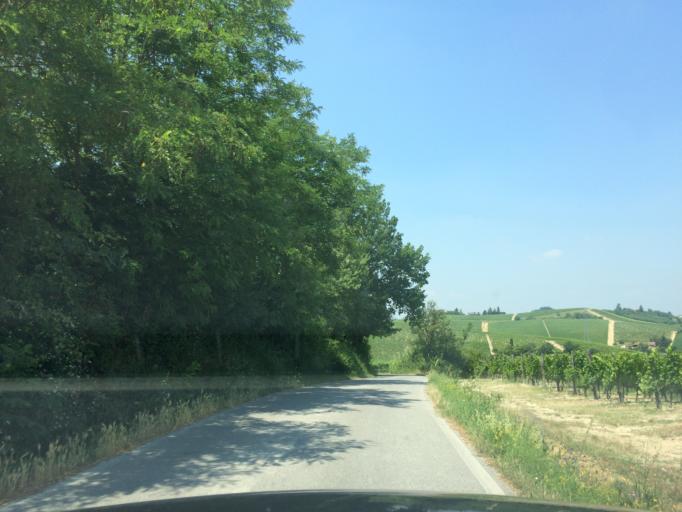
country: IT
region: Piedmont
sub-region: Provincia di Asti
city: Vaglio Serra
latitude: 44.7791
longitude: 8.3163
